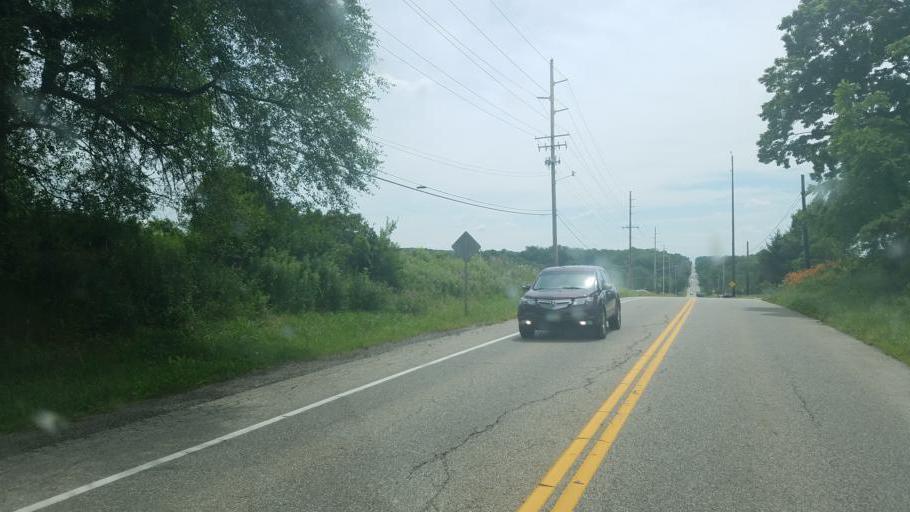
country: US
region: Ohio
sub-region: Geauga County
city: Bainbridge
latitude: 41.4063
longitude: -81.3253
